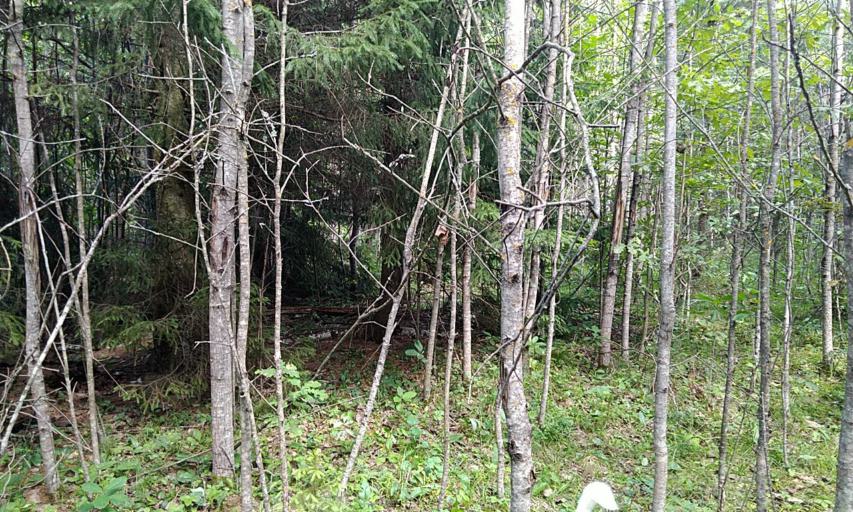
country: RU
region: Moskovskaya
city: Obolensk
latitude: 55.1038
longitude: 37.2047
